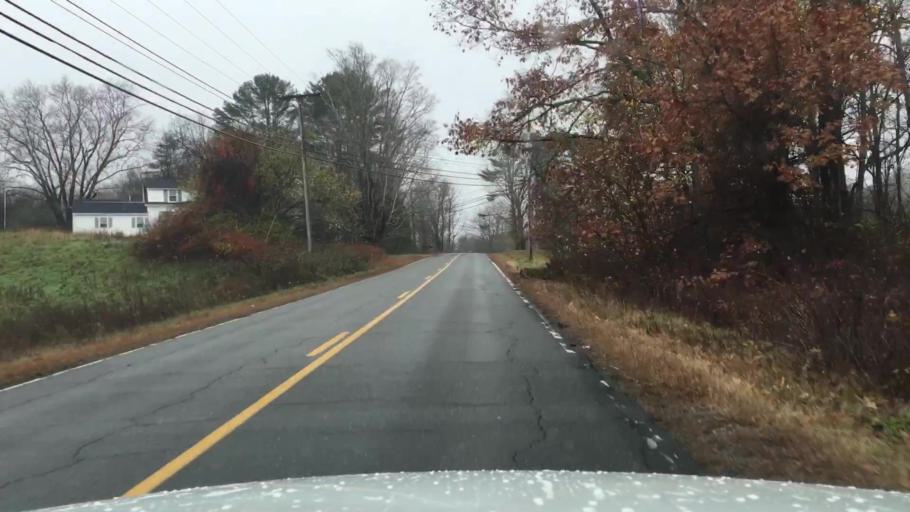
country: US
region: Maine
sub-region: Lincoln County
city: Waldoboro
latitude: 44.0697
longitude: -69.3593
